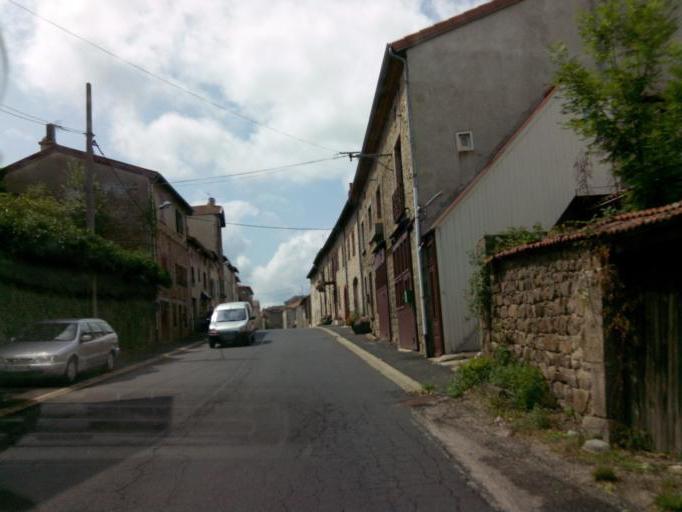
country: FR
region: Rhone-Alpes
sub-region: Departement de la Loire
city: Usson-en-Forez
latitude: 45.3591
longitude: 3.9582
